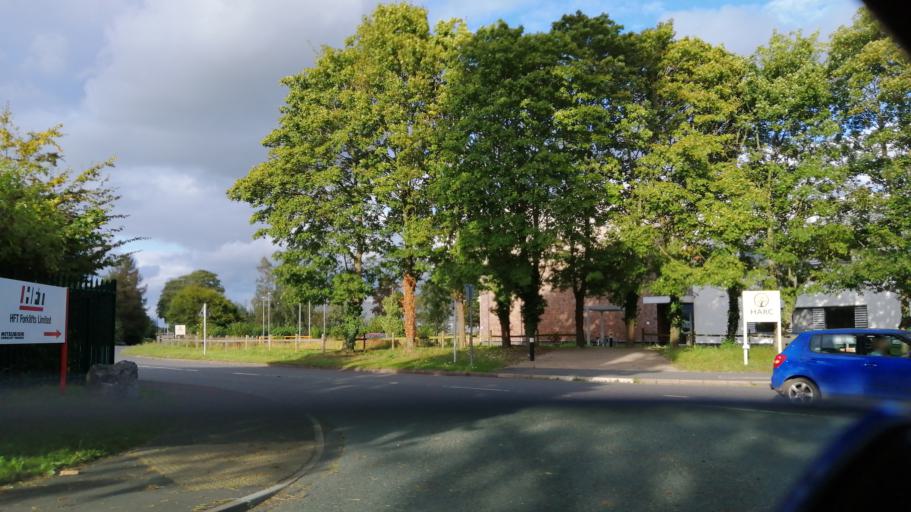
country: GB
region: England
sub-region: Herefordshire
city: Lower Bullingham
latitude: 52.0386
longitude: -2.6887
